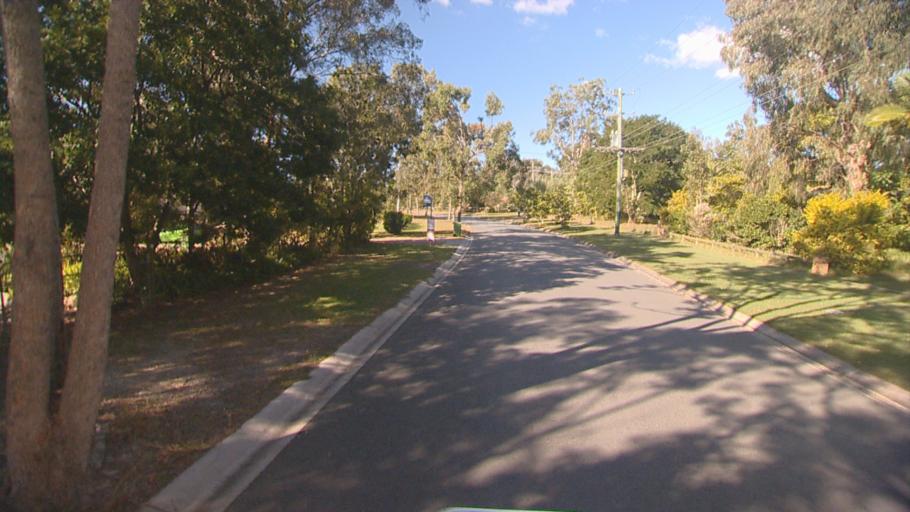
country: AU
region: Queensland
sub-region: Logan
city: Park Ridge South
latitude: -27.7053
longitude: 153.0161
